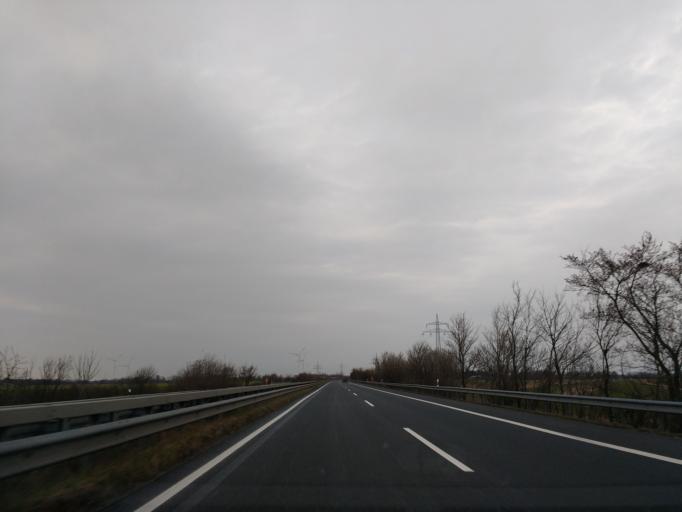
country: DE
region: Lower Saxony
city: Cuxhaven
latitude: 53.8015
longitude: 8.7073
